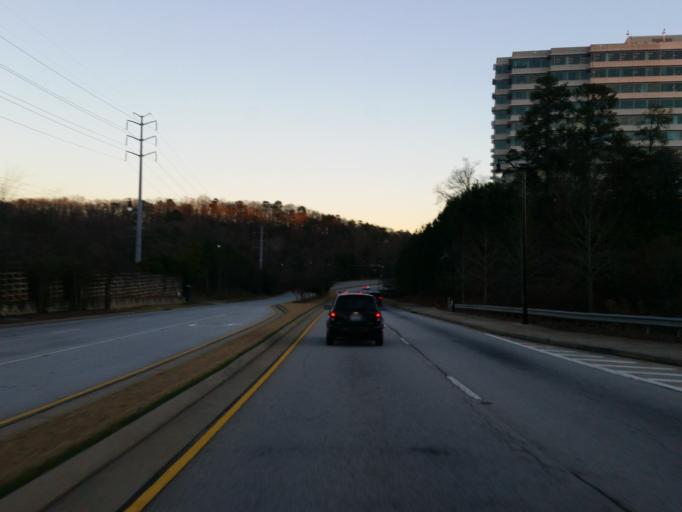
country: US
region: Georgia
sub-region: Cobb County
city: Vinings
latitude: 33.8860
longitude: -84.4544
